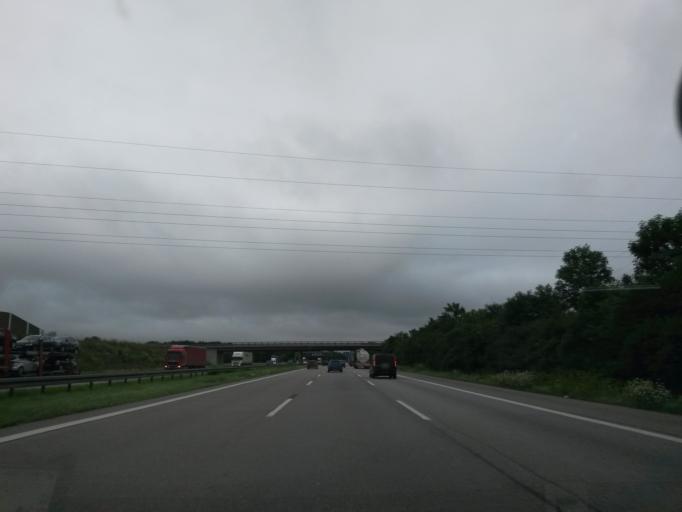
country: DE
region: Bavaria
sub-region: Upper Bavaria
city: Grasbrunn
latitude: 48.0770
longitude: 11.7317
